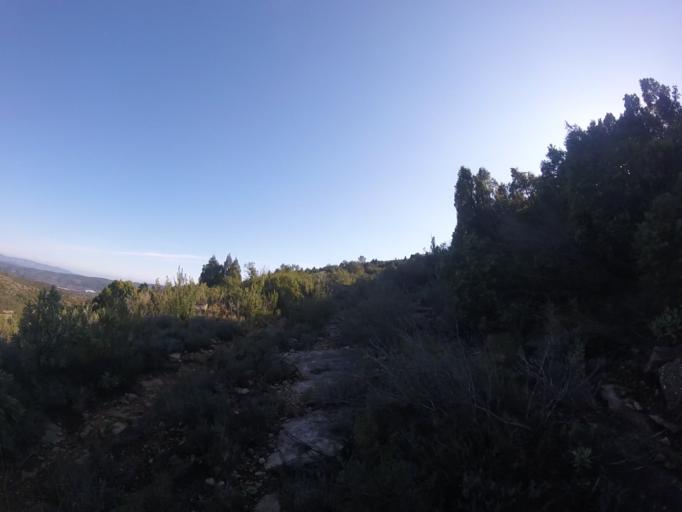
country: ES
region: Valencia
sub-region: Provincia de Castello
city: Sarratella
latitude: 40.2921
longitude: 0.0510
